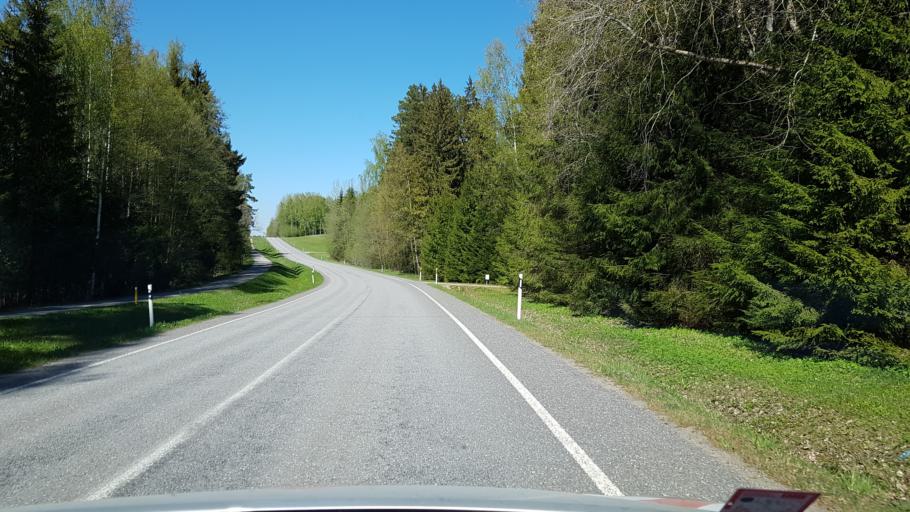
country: EE
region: Vorumaa
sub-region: Antsla vald
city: Vana-Antsla
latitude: 58.0255
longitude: 26.4399
